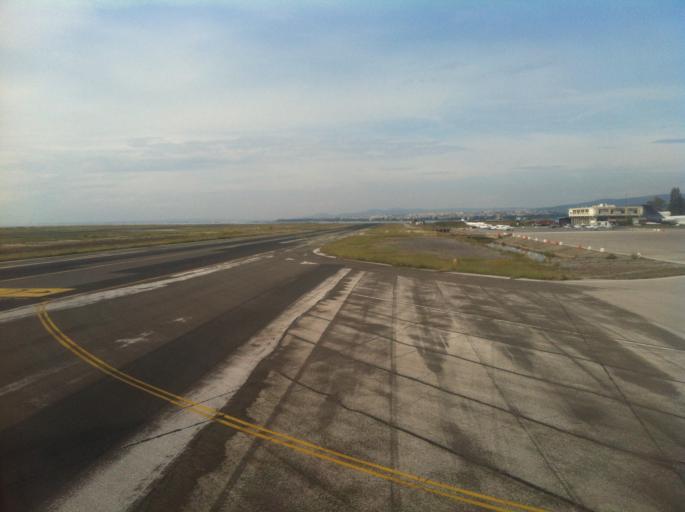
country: GR
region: Central Macedonia
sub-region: Nomos Thessalonikis
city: Neo Rysi
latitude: 40.5238
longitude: 22.9719
